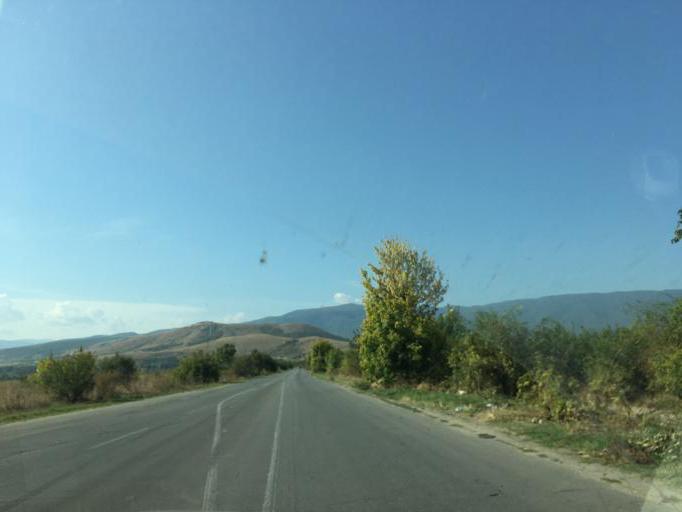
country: BG
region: Pazardzhik
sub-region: Obshtina Pazardzhik
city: Pazardzhik
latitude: 42.1381
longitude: 24.2982
